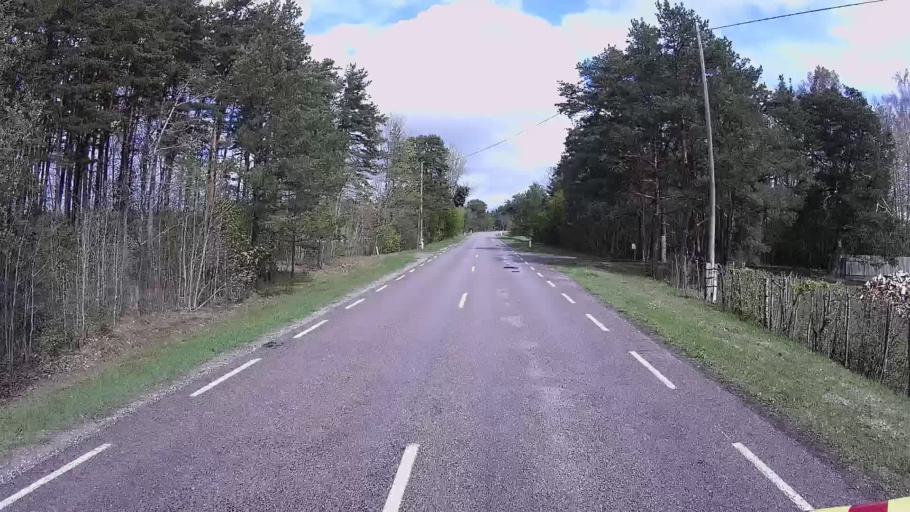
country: EE
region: Hiiumaa
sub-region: Kaerdla linn
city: Kardla
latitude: 58.7205
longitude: 22.6168
